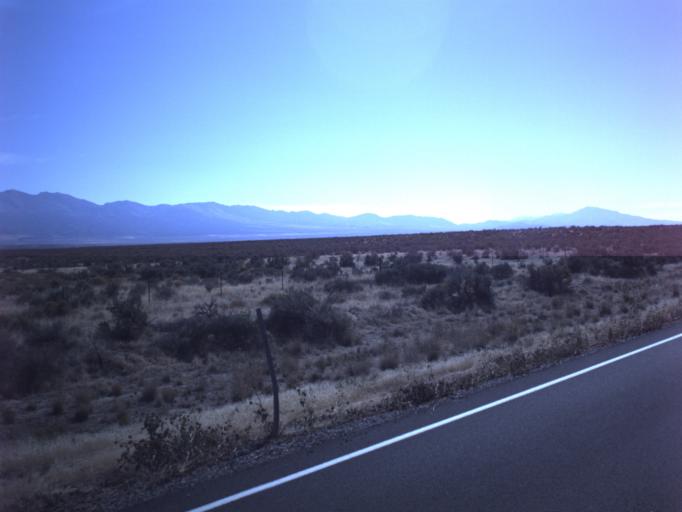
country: US
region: Utah
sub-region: Tooele County
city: Grantsville
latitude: 40.3417
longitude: -112.7449
